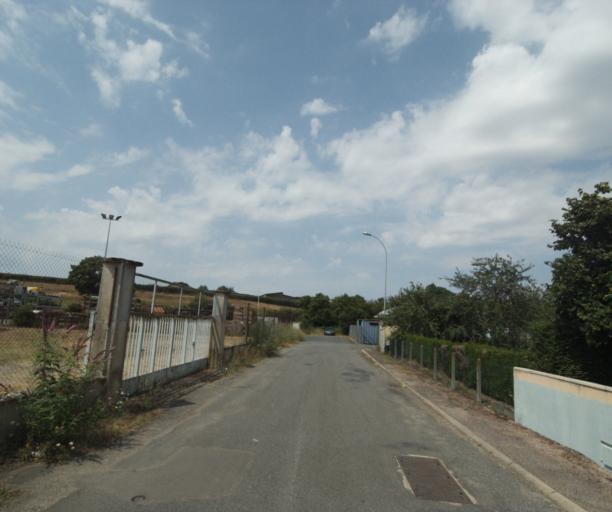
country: FR
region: Bourgogne
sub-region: Departement de Saone-et-Loire
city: Gueugnon
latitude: 46.5954
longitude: 4.0505
